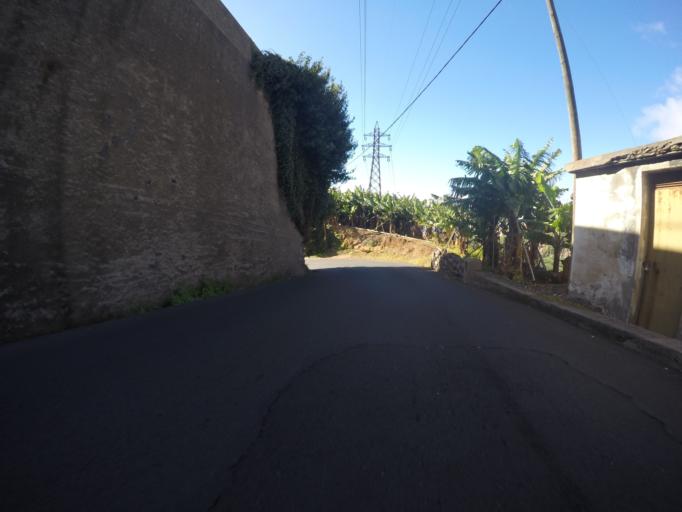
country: PT
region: Madeira
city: Camara de Lobos
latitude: 32.6493
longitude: -16.9655
